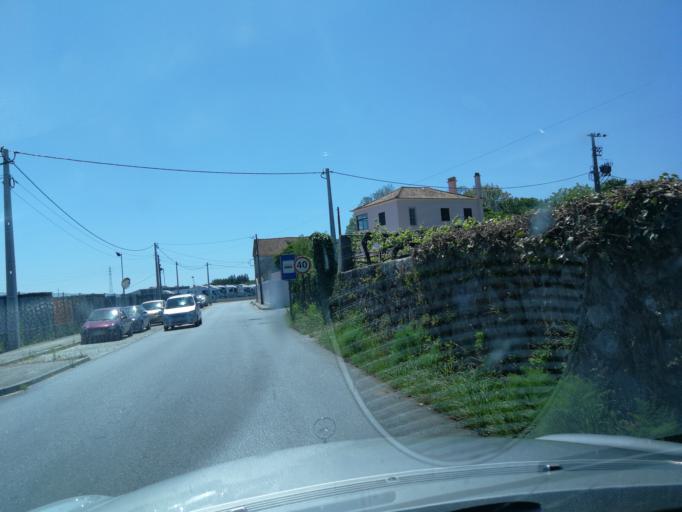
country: PT
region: Viana do Castelo
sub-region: Viana do Castelo
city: Meadela
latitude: 41.7137
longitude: -8.8006
